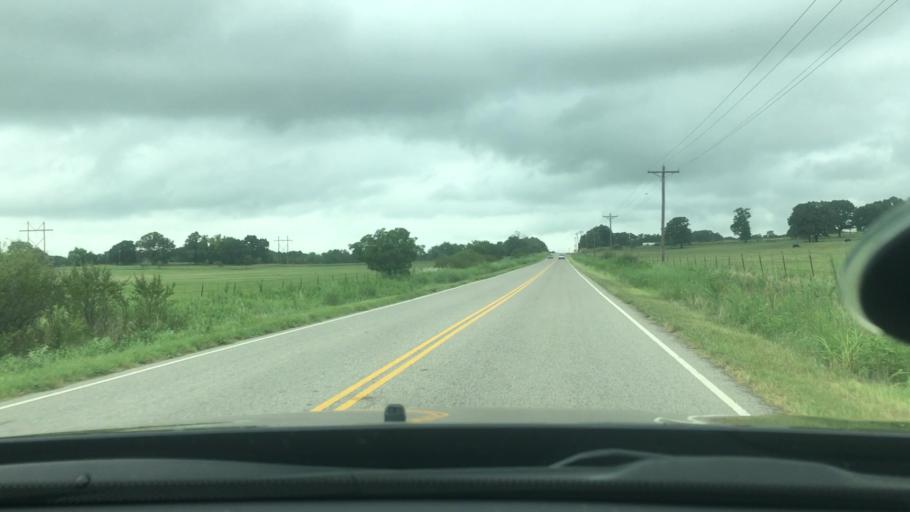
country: US
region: Oklahoma
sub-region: Bryan County
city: Calera
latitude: 33.9653
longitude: -96.5005
